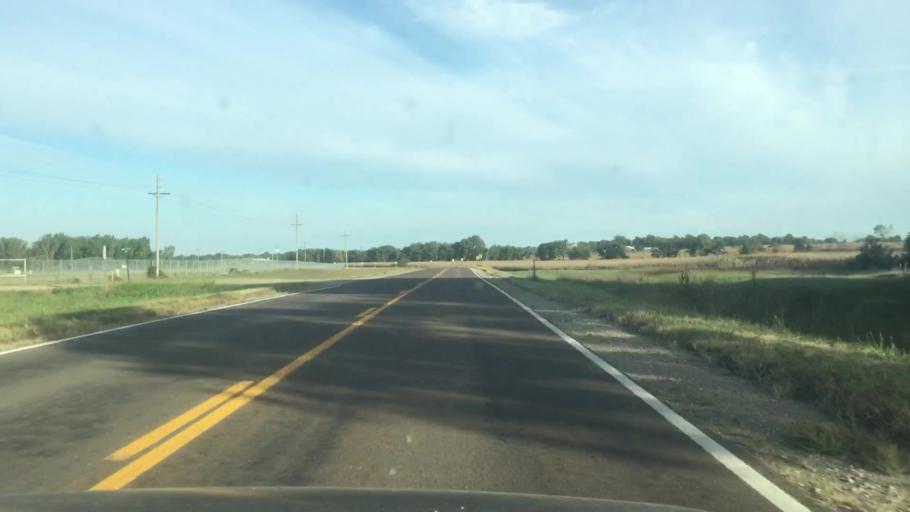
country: US
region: Nebraska
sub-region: Jefferson County
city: Fairbury
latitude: 40.1205
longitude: -97.1575
